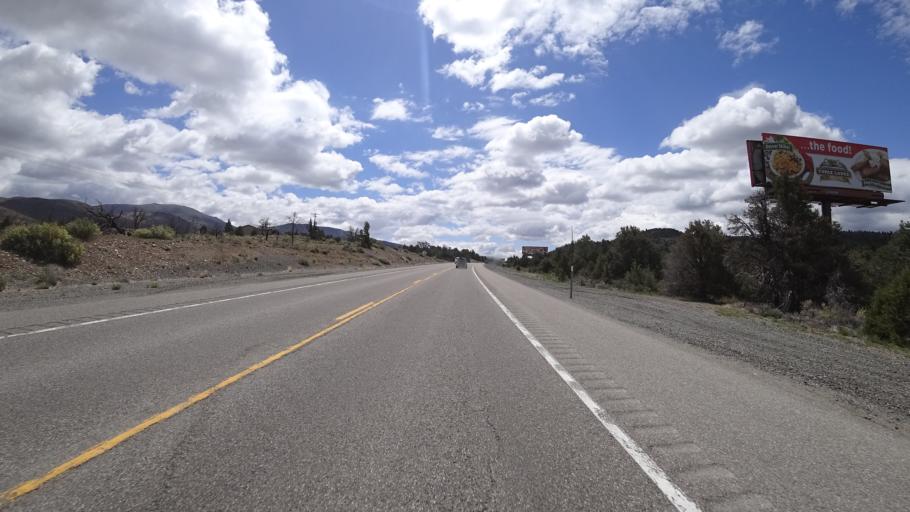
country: US
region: Nevada
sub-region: Douglas County
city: Gardnerville Ranchos
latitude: 38.8185
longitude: -119.6174
